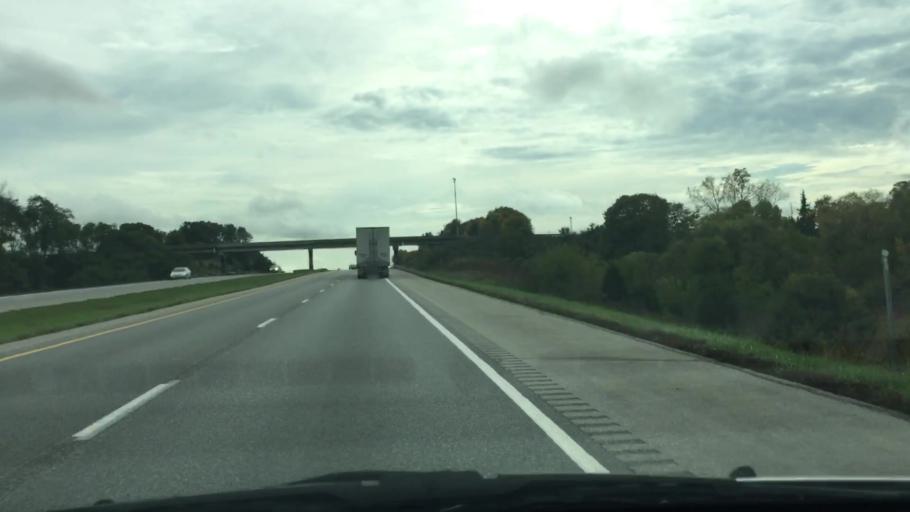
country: US
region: Iowa
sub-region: Warren County
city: Norwalk
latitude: 41.3900
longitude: -93.7809
